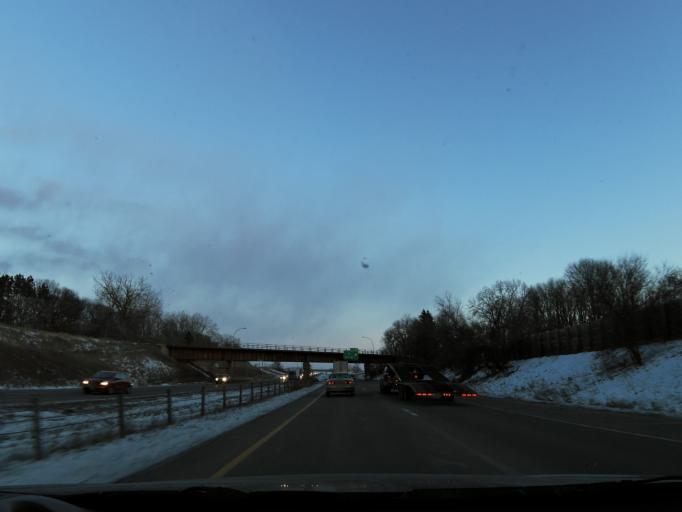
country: US
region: Minnesota
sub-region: Ramsey County
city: Little Canada
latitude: 45.0484
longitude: -93.1125
